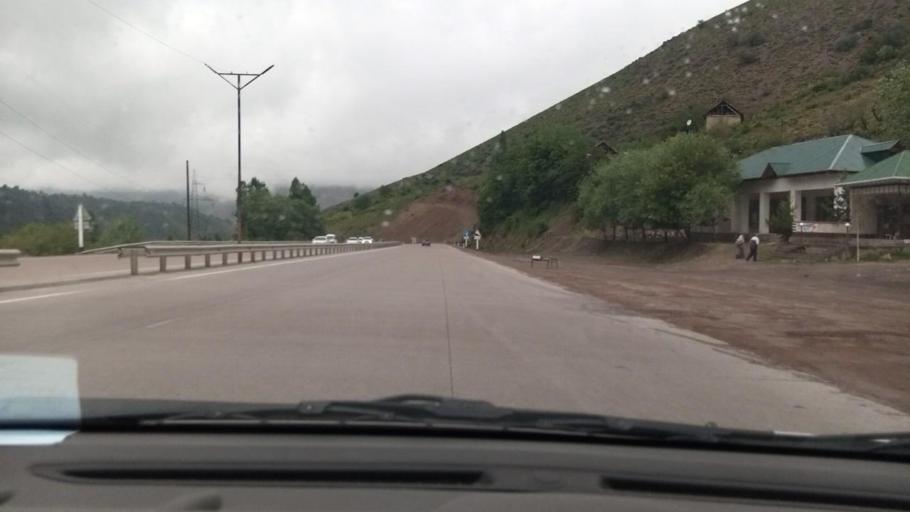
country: UZ
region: Toshkent
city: Angren
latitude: 41.1364
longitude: 70.4604
